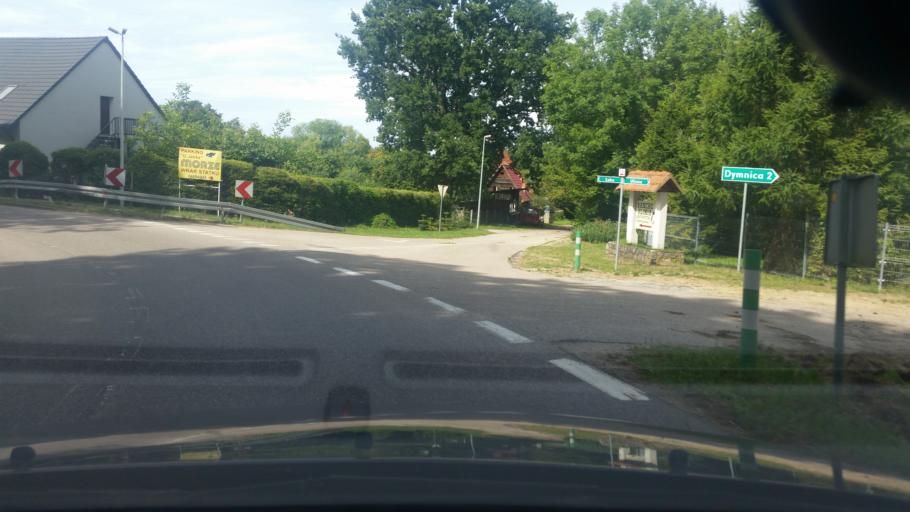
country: PL
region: Pomeranian Voivodeship
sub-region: Powiat leborski
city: Leba
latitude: 54.7560
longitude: 17.7072
